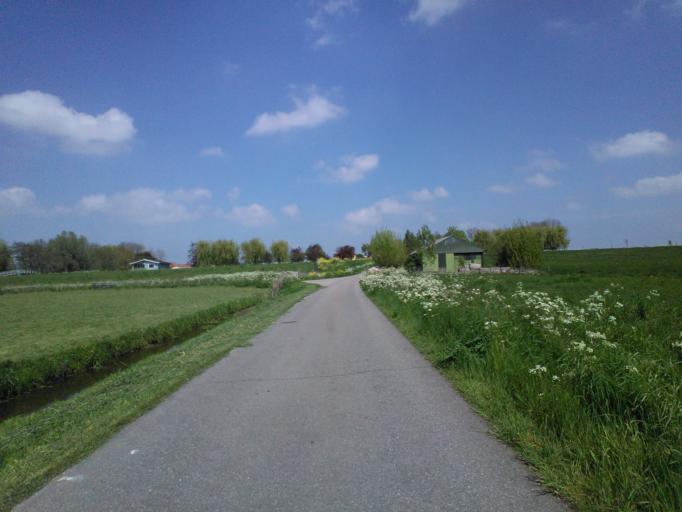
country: NL
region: South Holland
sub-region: Gemeente Boskoop
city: Boskoop
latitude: 52.1010
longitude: 4.6027
